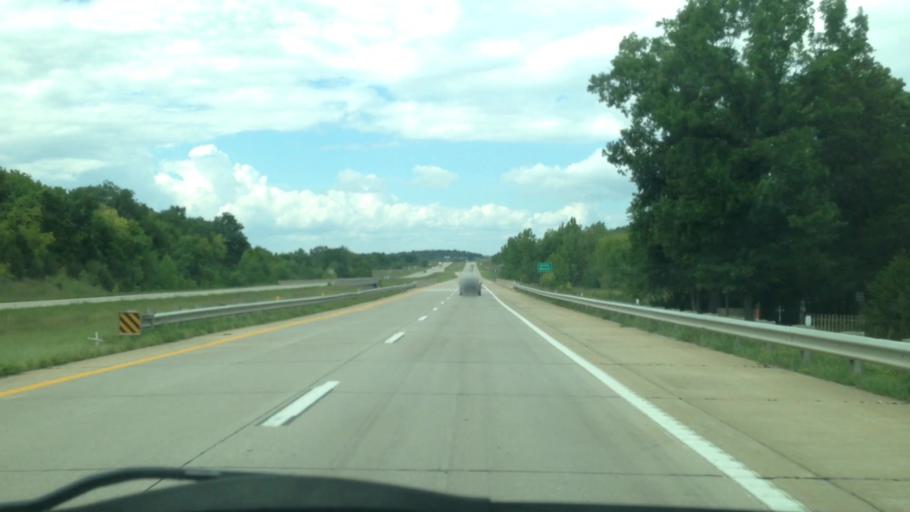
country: US
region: Missouri
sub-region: Pike County
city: Bowling Green
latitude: 39.4040
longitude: -91.2449
